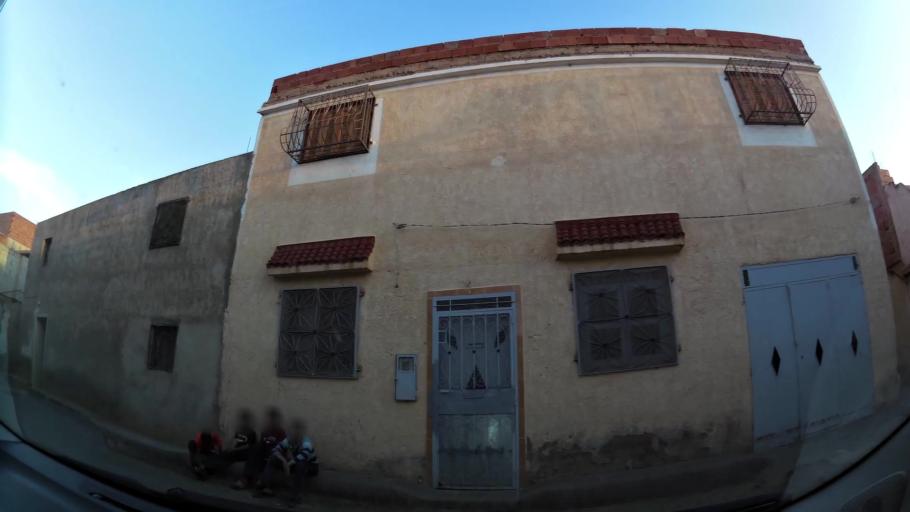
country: MA
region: Oriental
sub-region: Oujda-Angad
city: Oujda
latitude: 34.6999
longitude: -1.9244
